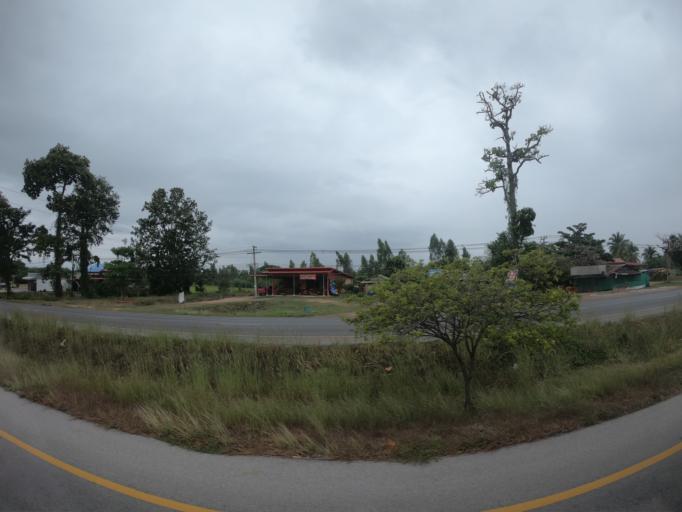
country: TH
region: Maha Sarakham
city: Kut Rang
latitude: 16.0542
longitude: 103.0088
